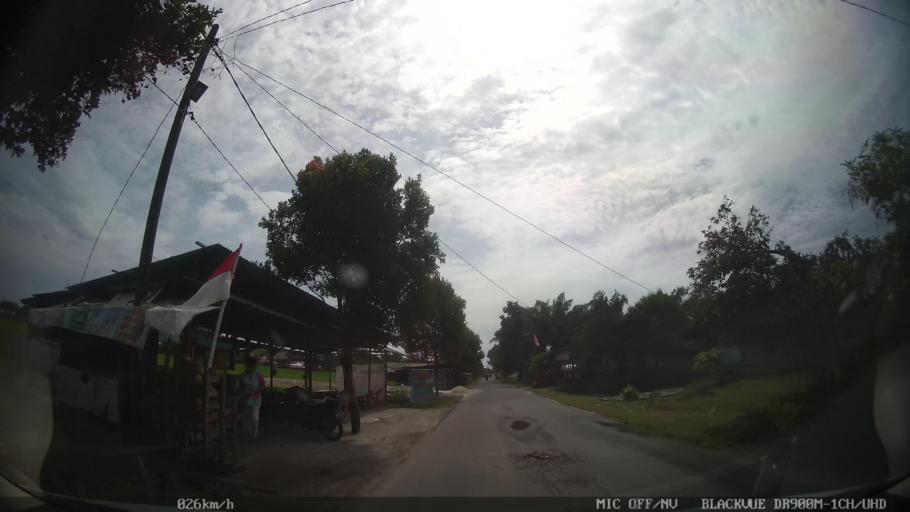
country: ID
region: North Sumatra
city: Percut
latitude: 3.6198
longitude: 98.7921
